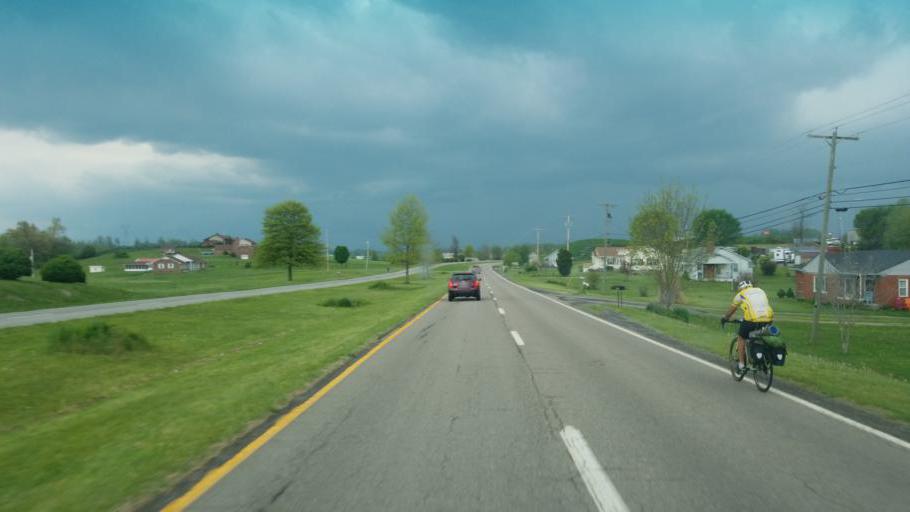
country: US
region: Virginia
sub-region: Washington County
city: Glade Spring
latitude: 36.7717
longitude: -81.7713
